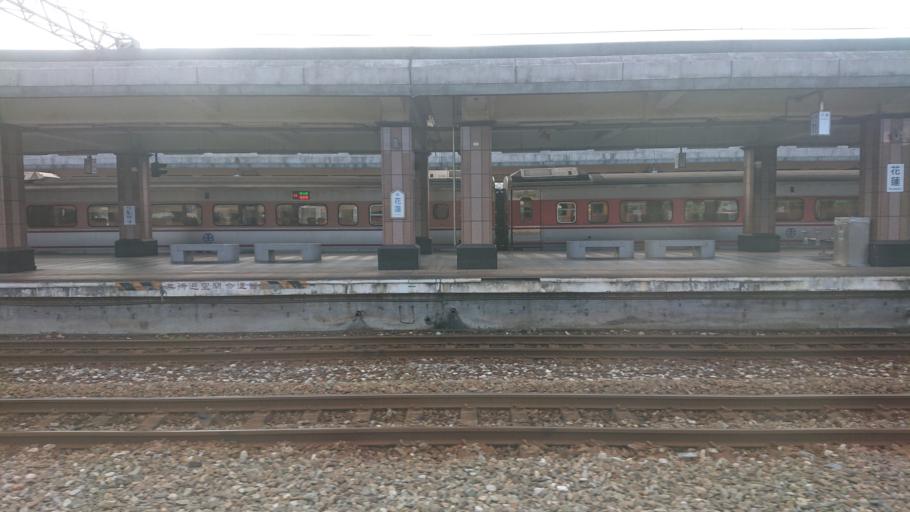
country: TW
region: Taiwan
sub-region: Hualien
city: Hualian
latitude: 23.9921
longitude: 121.6007
